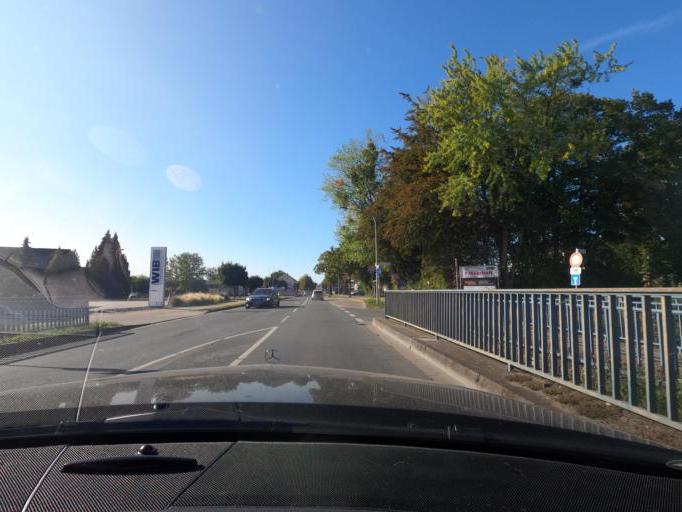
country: DE
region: North Rhine-Westphalia
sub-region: Regierungsbezirk Arnsberg
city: Werl
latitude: 51.5639
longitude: 7.8977
